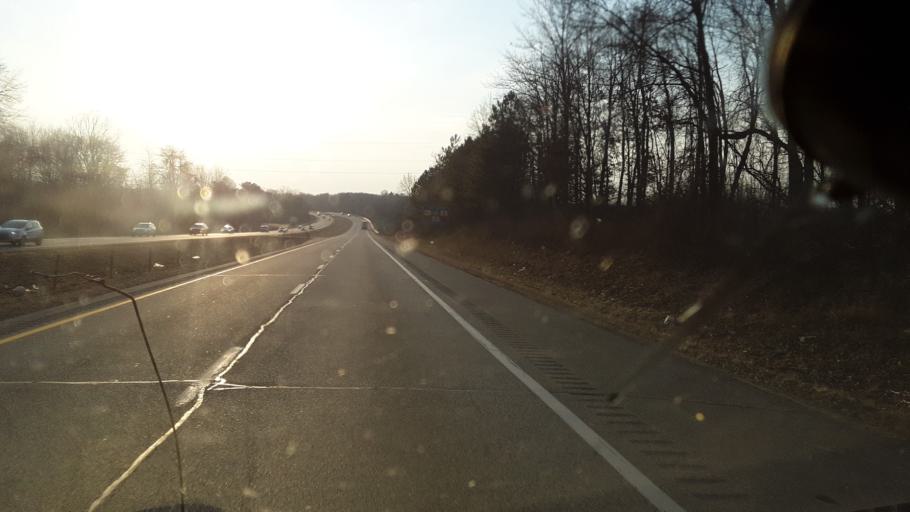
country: US
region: Ohio
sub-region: Portage County
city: Brimfield
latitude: 41.1063
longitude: -81.3594
